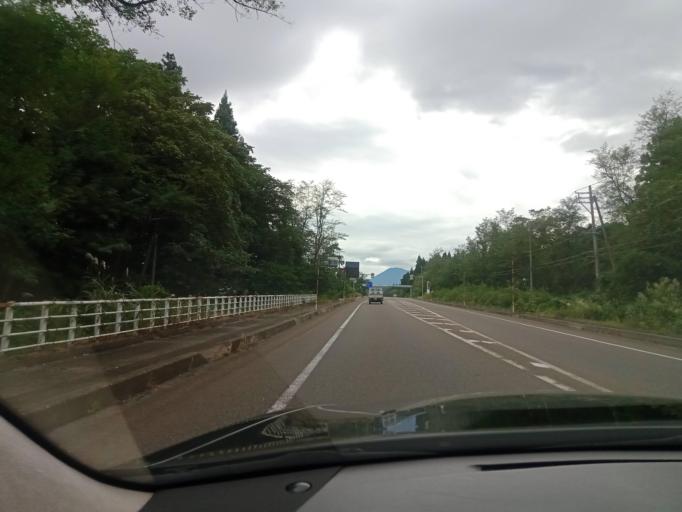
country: JP
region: Niigata
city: Arai
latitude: 36.9631
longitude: 138.2233
